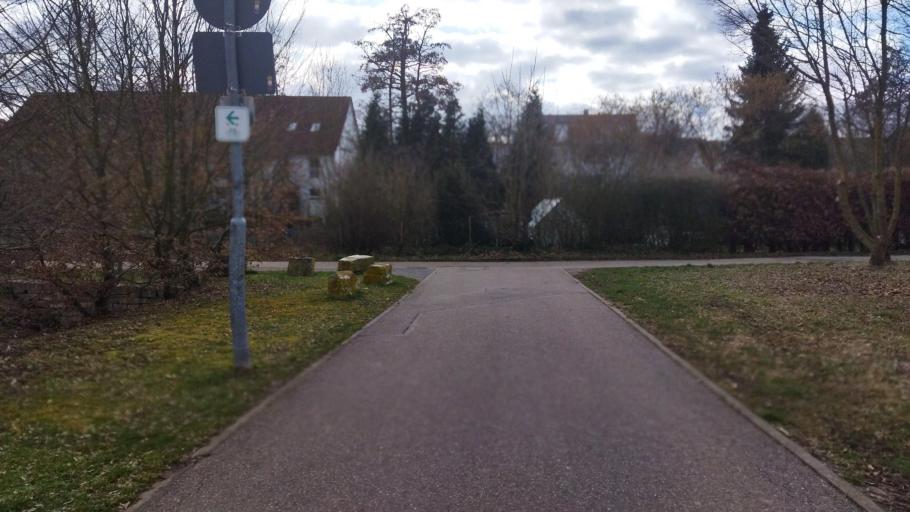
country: DE
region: Baden-Wuerttemberg
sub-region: Regierungsbezirk Stuttgart
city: Freudental
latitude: 49.0123
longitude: 9.0589
